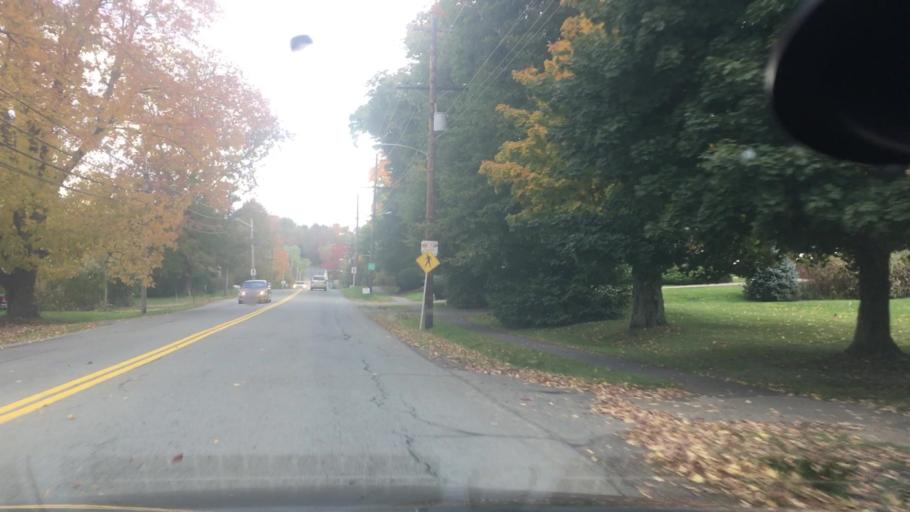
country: CA
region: Nova Scotia
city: Windsor
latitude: 44.9829
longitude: -64.1305
